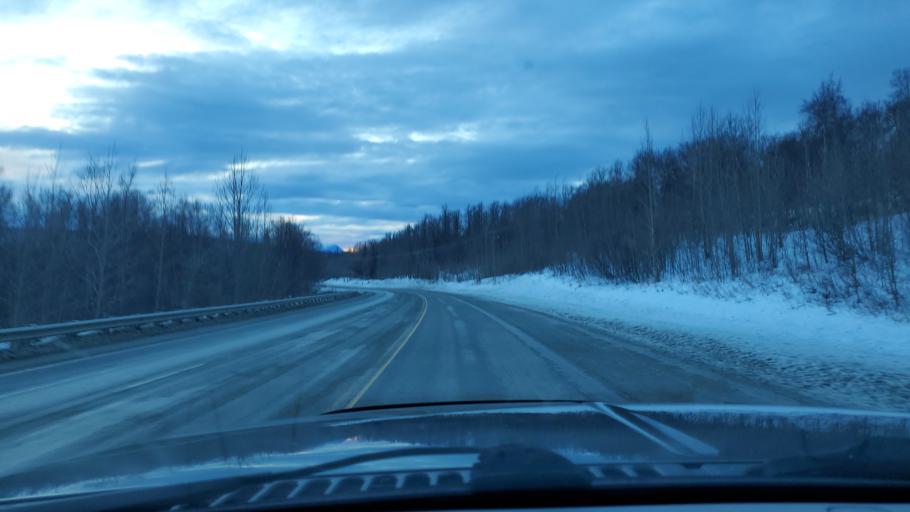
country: US
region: Alaska
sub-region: Matanuska-Susitna Borough
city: Lazy Mountain
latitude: 61.6876
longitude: -148.9824
